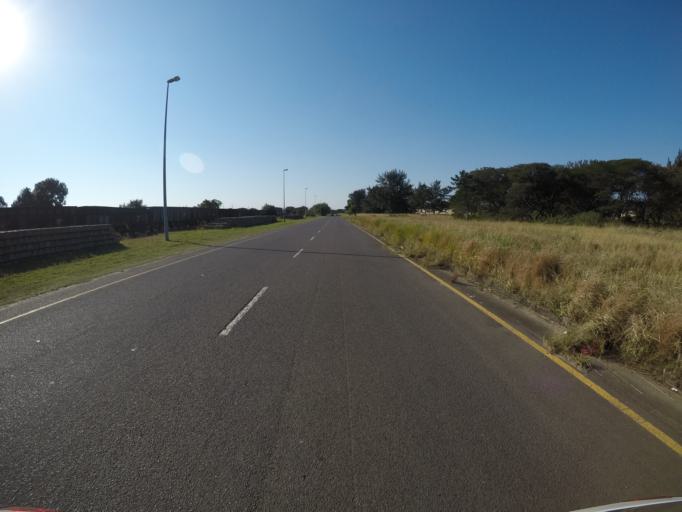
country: ZA
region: KwaZulu-Natal
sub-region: uThungulu District Municipality
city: Richards Bay
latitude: -28.7900
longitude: 32.0784
